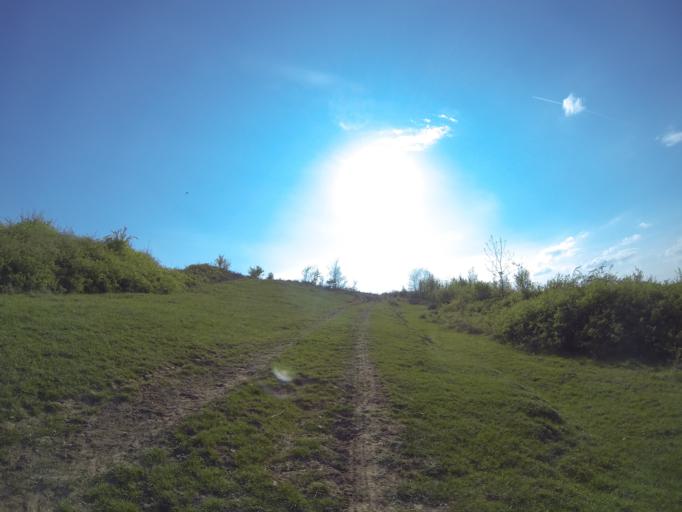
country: RO
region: Gorj
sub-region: Comuna Crusetu
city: Crusetu
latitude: 44.6013
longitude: 23.6334
